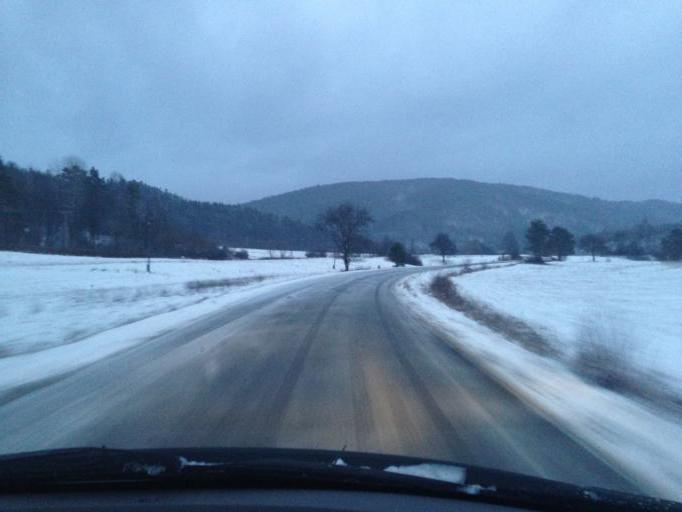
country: PL
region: Subcarpathian Voivodeship
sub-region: Powiat jasielski
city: Krempna
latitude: 49.5034
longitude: 21.5260
